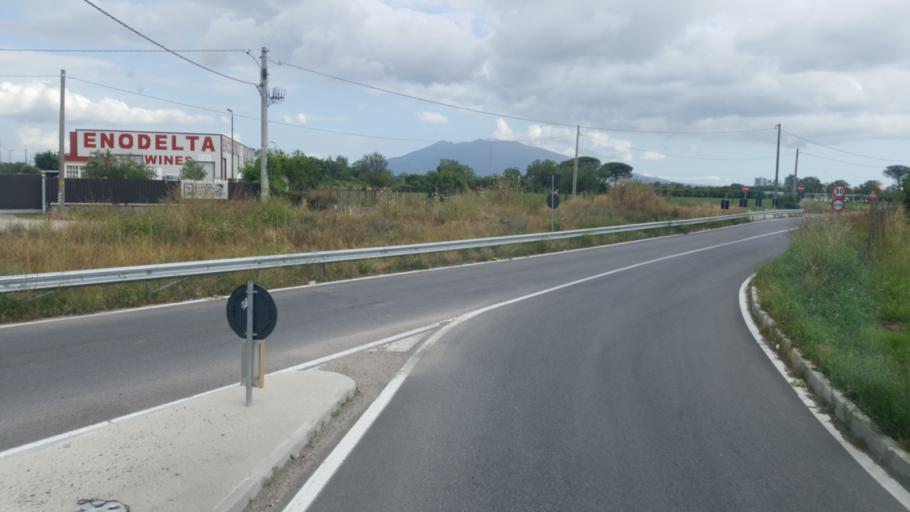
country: IT
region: Campania
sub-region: Provincia di Napoli
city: Acerra
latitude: 40.9733
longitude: 14.3905
